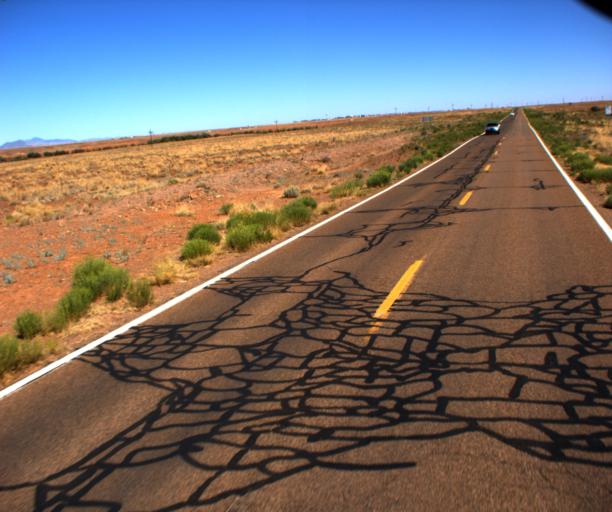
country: US
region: Arizona
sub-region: Coconino County
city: LeChee
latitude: 35.2712
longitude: -110.9755
